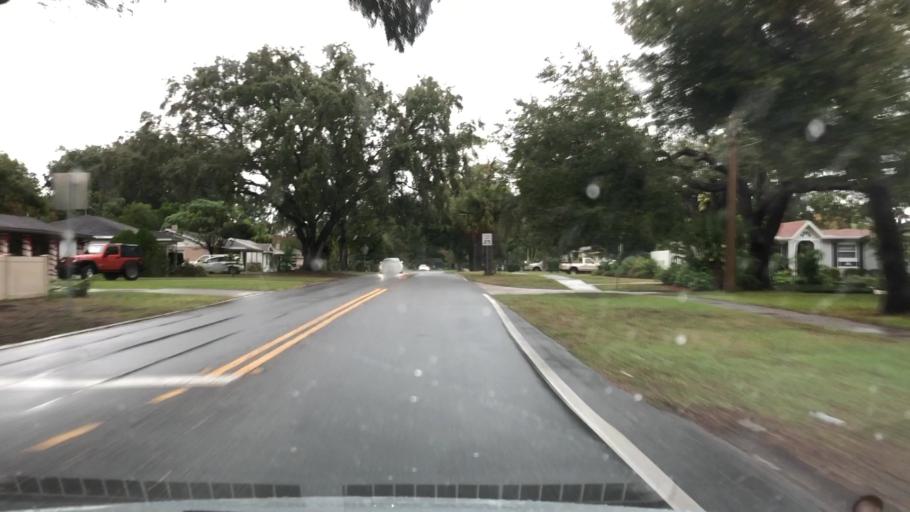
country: US
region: Florida
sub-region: Orange County
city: Orlando
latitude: 28.5316
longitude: -81.3476
